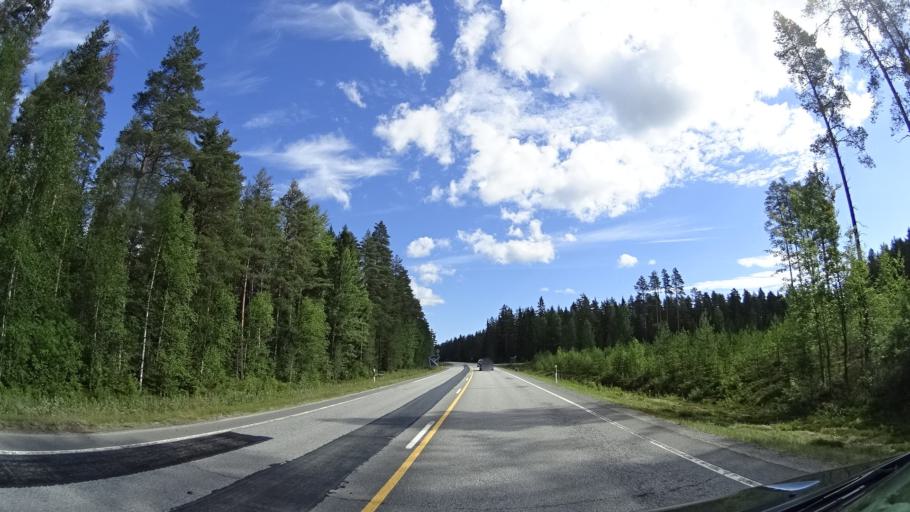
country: FI
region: Pirkanmaa
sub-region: Luoteis-Pirkanmaa
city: Kihnioe
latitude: 62.1326
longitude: 23.1356
